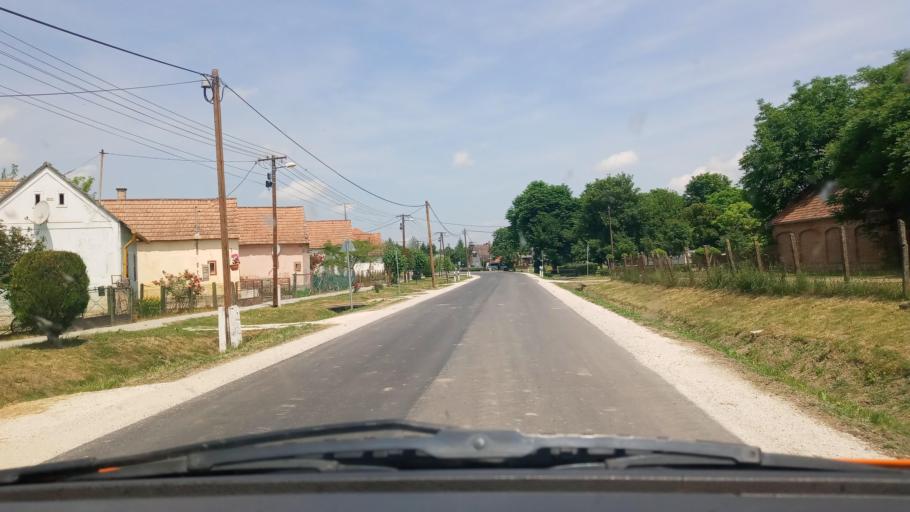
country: HU
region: Baranya
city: Szigetvar
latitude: 45.9601
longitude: 17.6587
